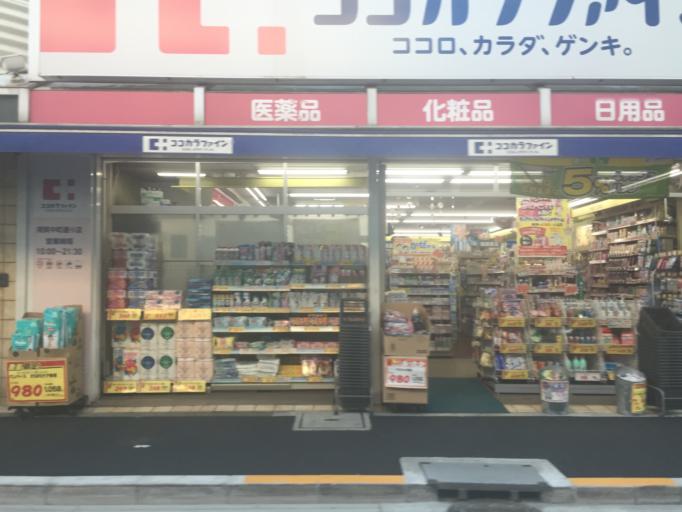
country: JP
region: Tokyo
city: Tokyo
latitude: 35.6196
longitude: 139.6417
